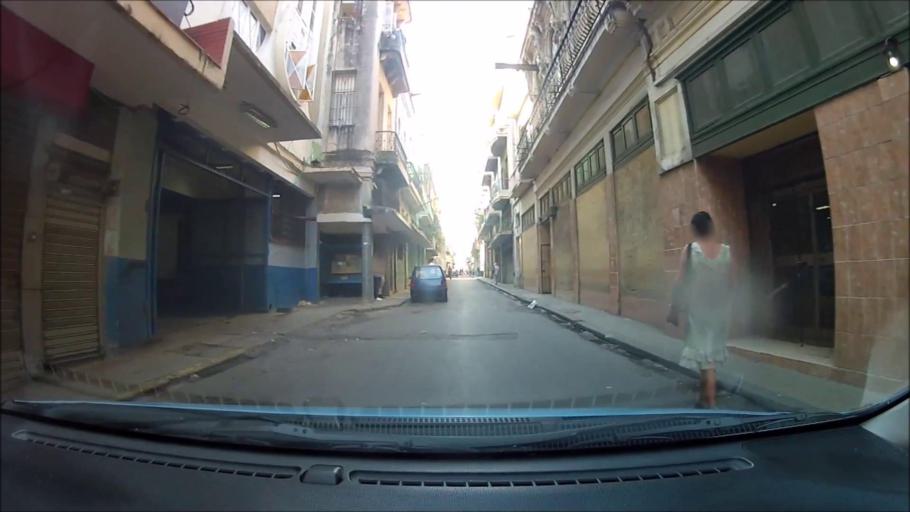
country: CU
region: La Habana
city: Centro Habana
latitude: 23.1370
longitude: -82.3643
